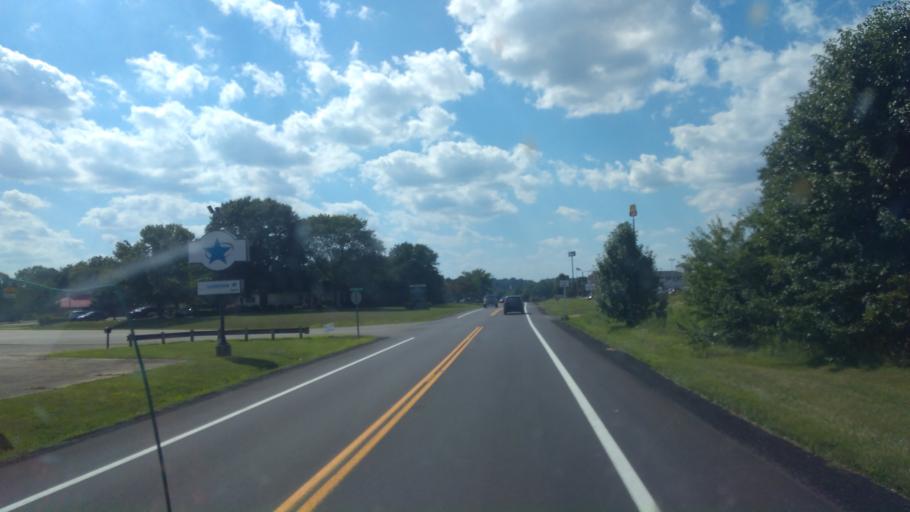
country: US
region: Ohio
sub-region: Tuscarawas County
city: Strasburg
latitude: 40.6391
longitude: -81.4410
